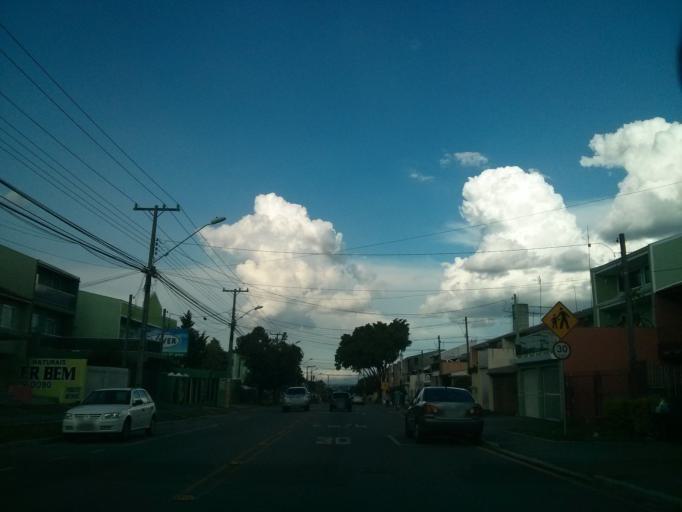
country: BR
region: Parana
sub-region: Sao Jose Dos Pinhais
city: Sao Jose dos Pinhais
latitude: -25.5142
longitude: -49.2425
